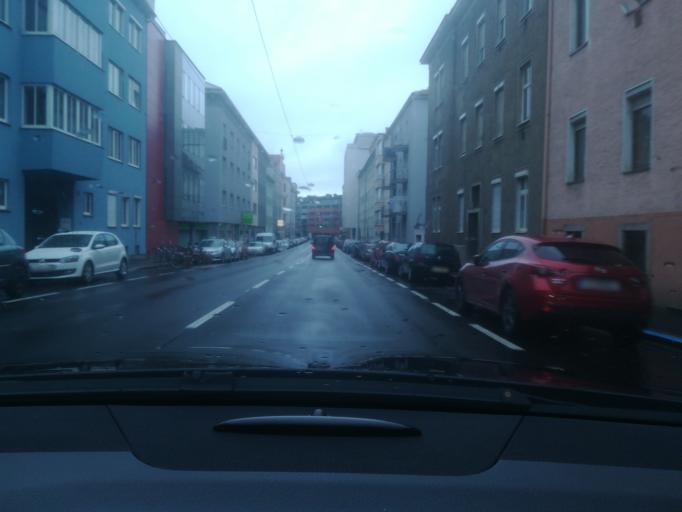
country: AT
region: Upper Austria
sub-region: Linz Stadt
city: Linz
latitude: 48.2958
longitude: 14.2842
